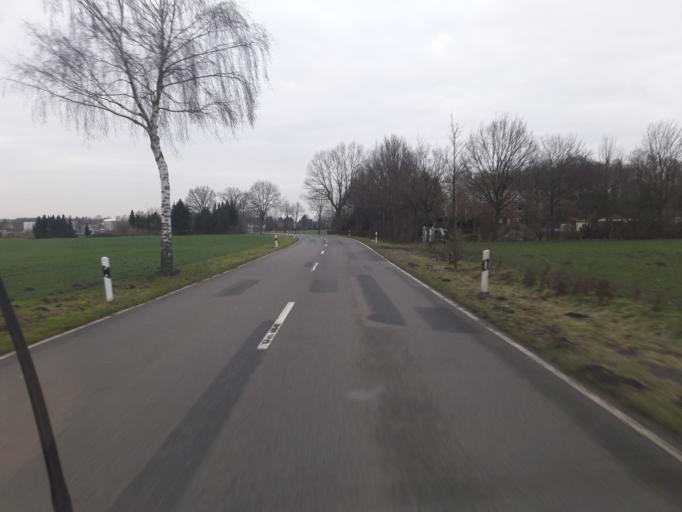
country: DE
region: Lower Saxony
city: Warmsen
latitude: 52.4452
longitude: 8.8559
